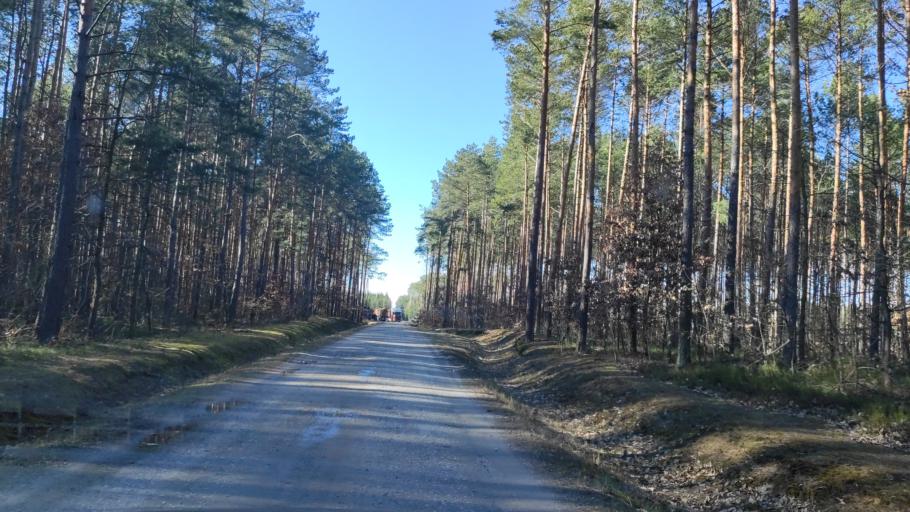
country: PL
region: Masovian Voivodeship
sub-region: Powiat radomski
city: Jedlnia-Letnisko
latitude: 51.4629
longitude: 21.3225
